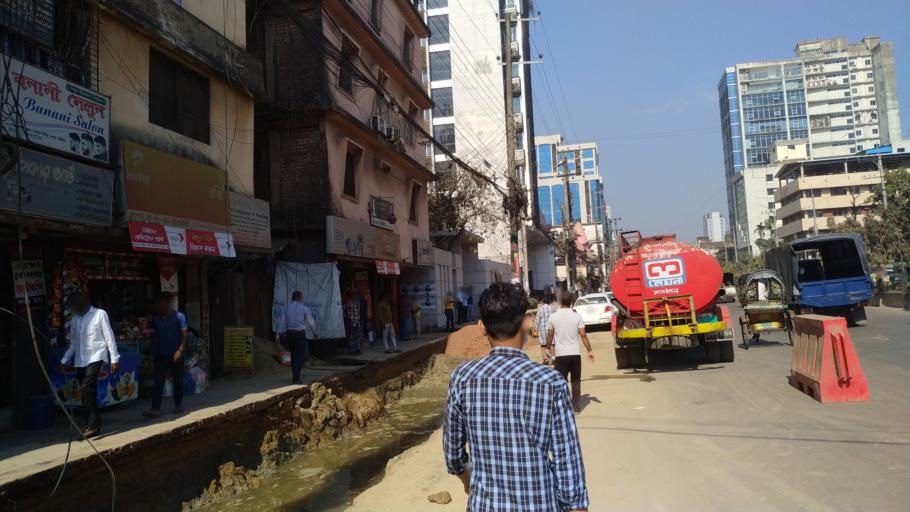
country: BD
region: Chittagong
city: Chittagong
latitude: 22.3200
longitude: 91.8119
